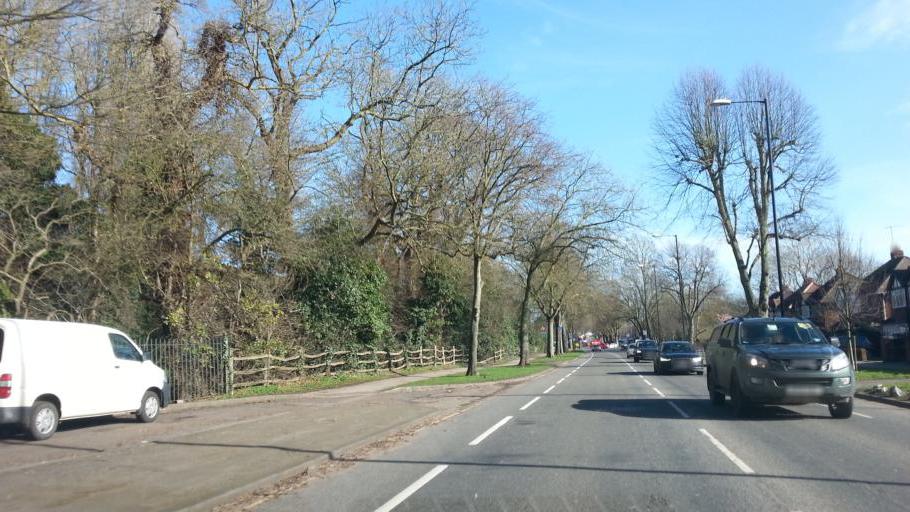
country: GB
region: England
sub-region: Coventry
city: Keresley
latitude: 52.4188
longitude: -1.5486
